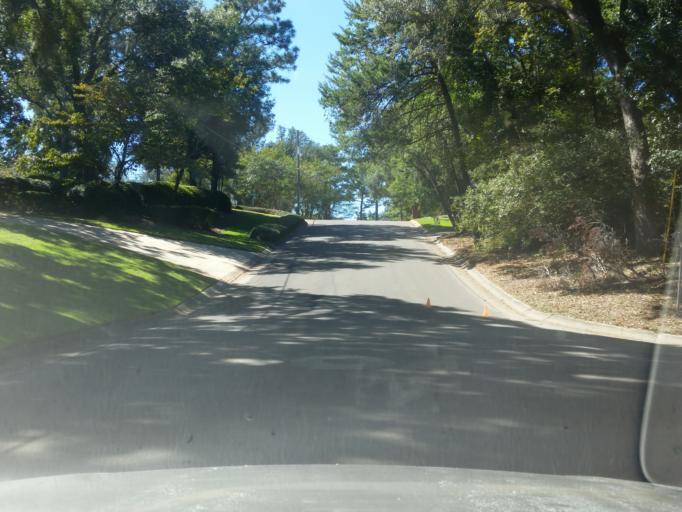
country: US
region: Florida
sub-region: Escambia County
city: East Pensacola Heights
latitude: 30.4728
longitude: -87.1669
